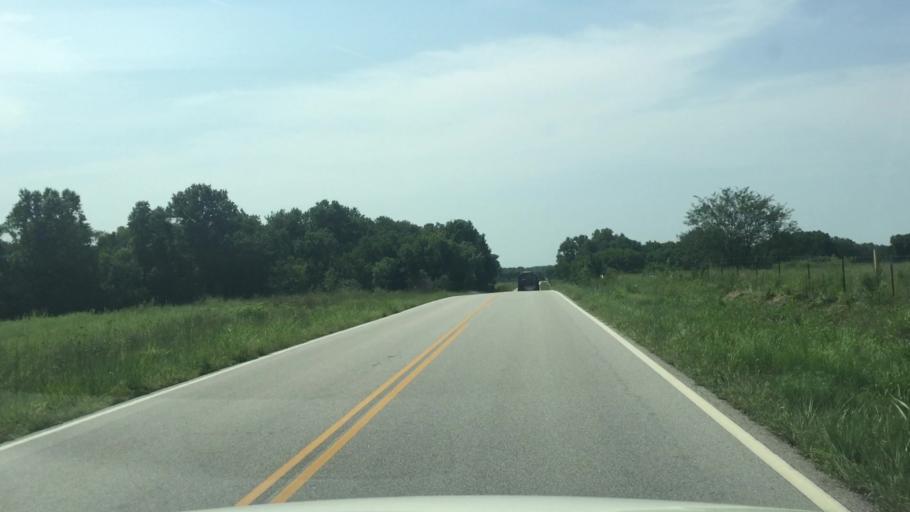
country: US
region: Kansas
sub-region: Montgomery County
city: Cherryvale
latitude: 37.2045
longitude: -95.5577
